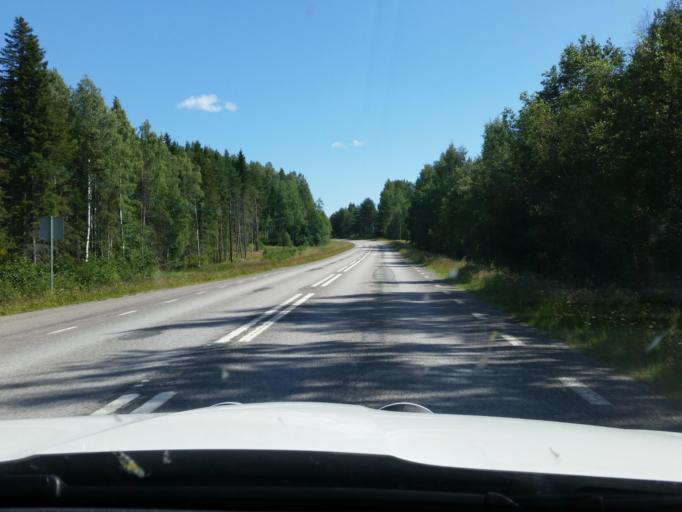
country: SE
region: Norrbotten
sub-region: Alvsbyns Kommun
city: AElvsbyn
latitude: 65.6779
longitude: 20.7554
